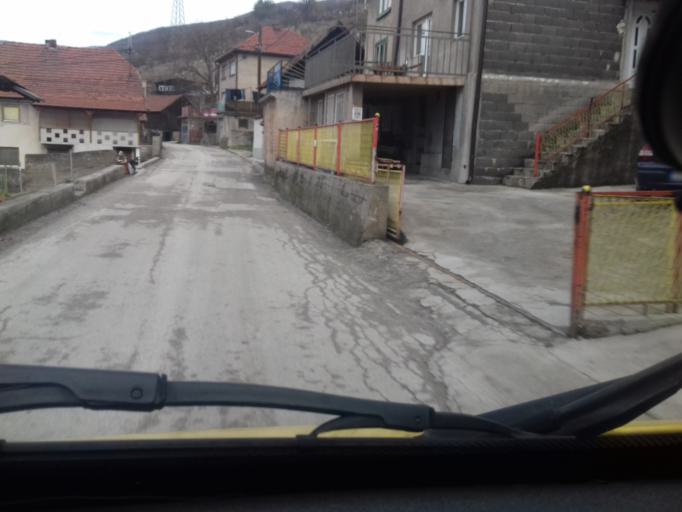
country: BA
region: Federation of Bosnia and Herzegovina
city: Zenica
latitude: 44.2320
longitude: 17.9092
